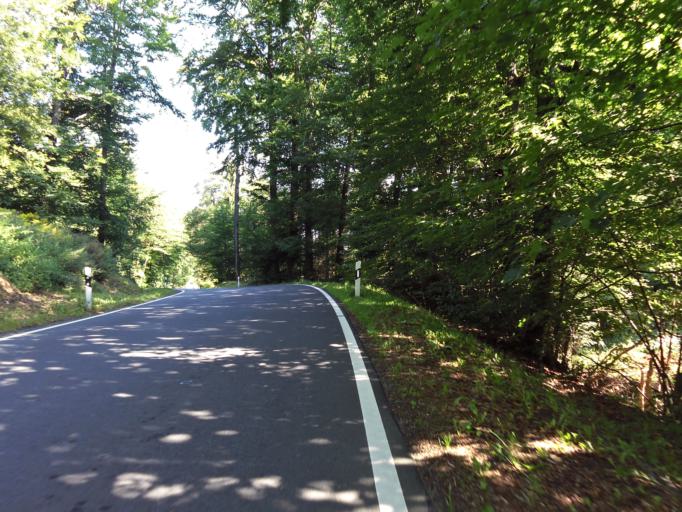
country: DE
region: Hesse
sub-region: Regierungsbezirk Darmstadt
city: Lindenfels
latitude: 49.6982
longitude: 8.7221
